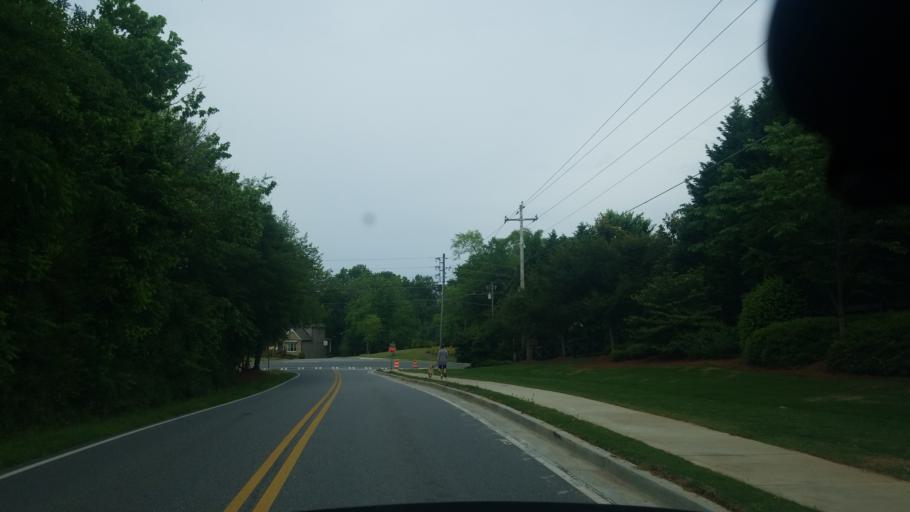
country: US
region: Georgia
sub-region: Gwinnett County
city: Suwanee
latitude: 34.1171
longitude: -84.1292
